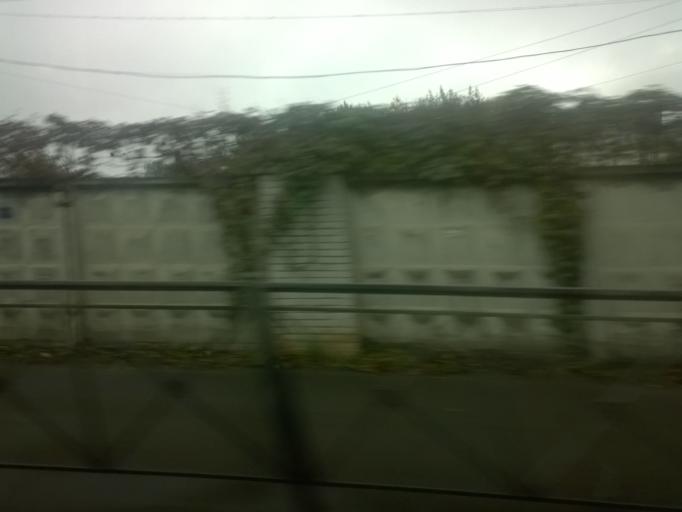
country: RU
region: St.-Petersburg
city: Avtovo
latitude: 59.8588
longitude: 30.2594
